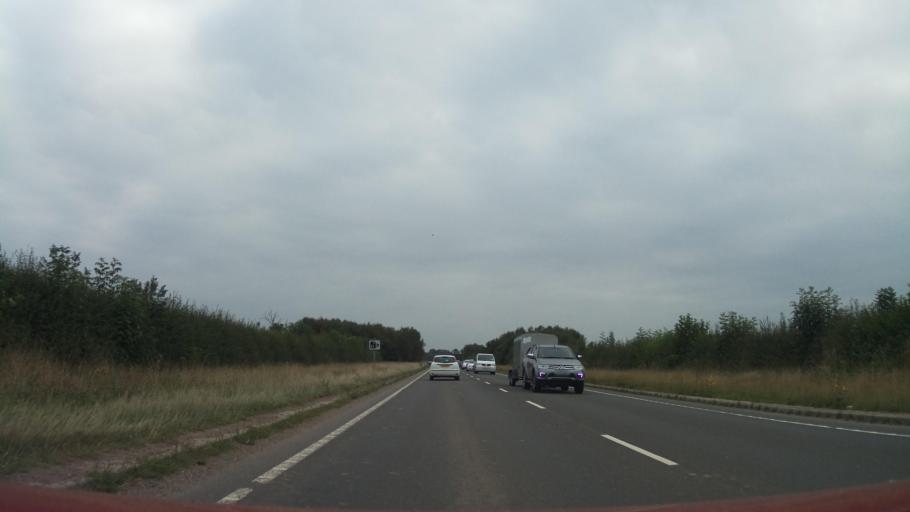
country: GB
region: England
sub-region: Shropshire
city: Stoke upon Tern
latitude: 52.8757
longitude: -2.5529
